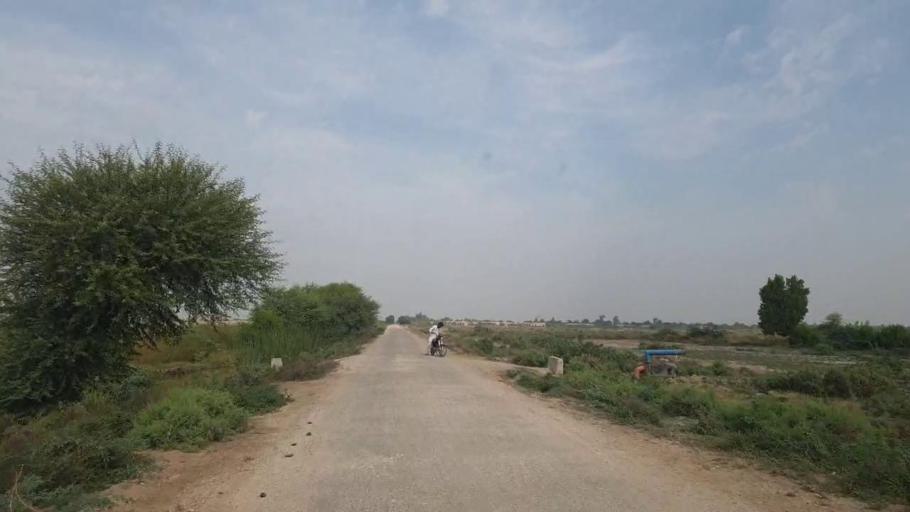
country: PK
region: Sindh
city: Rajo Khanani
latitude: 24.9824
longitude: 68.9951
